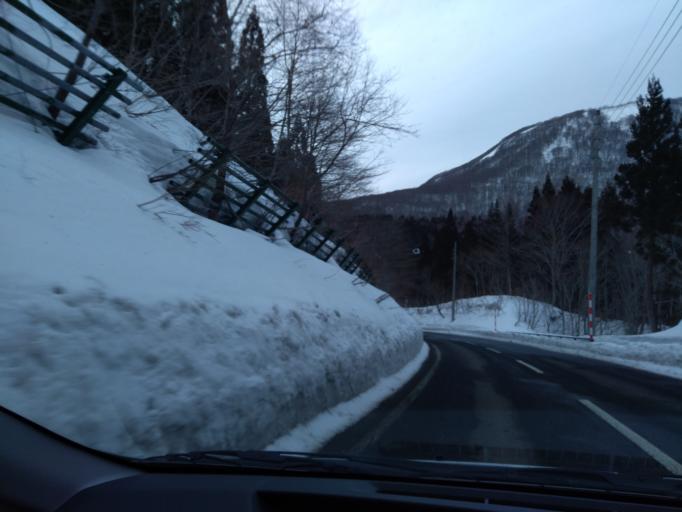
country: JP
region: Iwate
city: Kitakami
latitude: 39.2366
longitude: 140.9159
